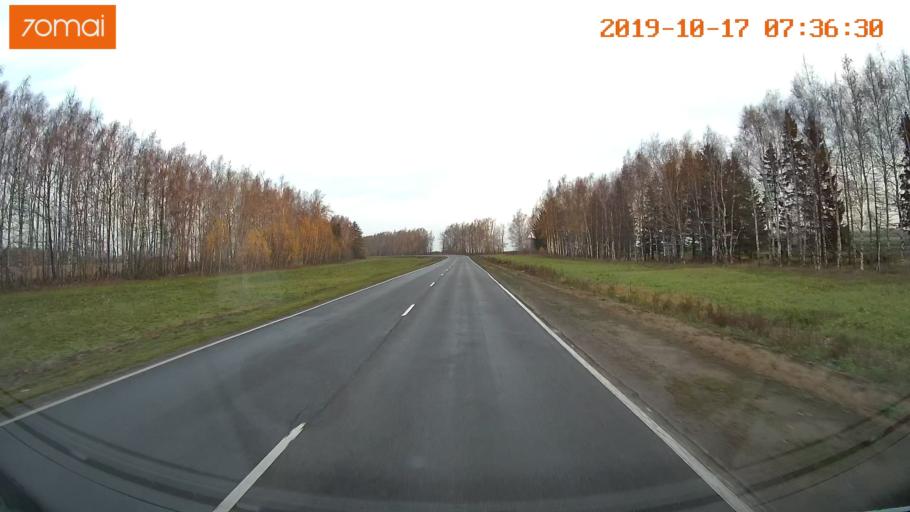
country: RU
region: Ivanovo
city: Gavrilov Posad
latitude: 56.4398
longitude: 39.9152
